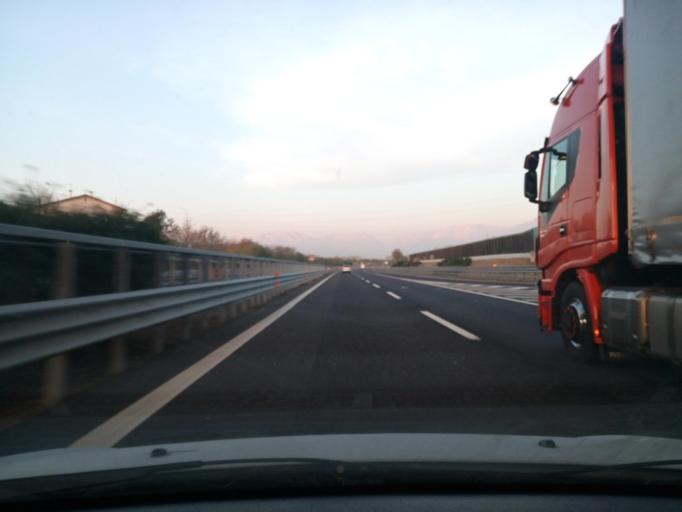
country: IT
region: Veneto
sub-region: Provincia di Vicenza
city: Villaverla
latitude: 45.6686
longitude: 11.4817
